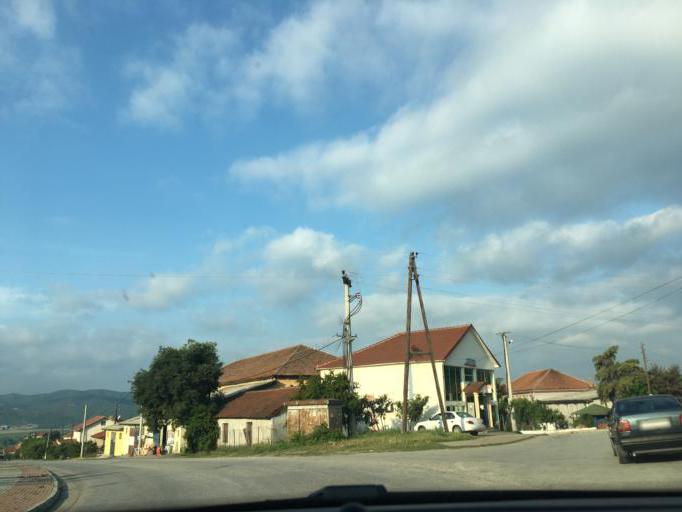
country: MK
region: Valandovo
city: Valandovo
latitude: 41.3192
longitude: 22.5665
